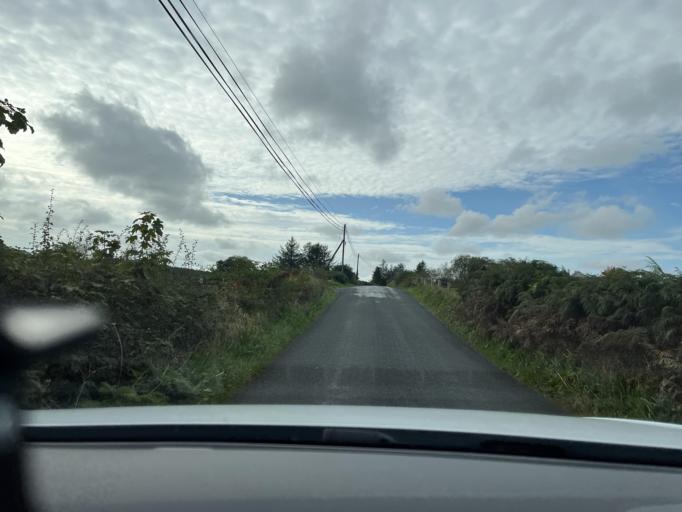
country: IE
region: Connaught
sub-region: Roscommon
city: Boyle
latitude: 54.0182
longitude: -8.3696
